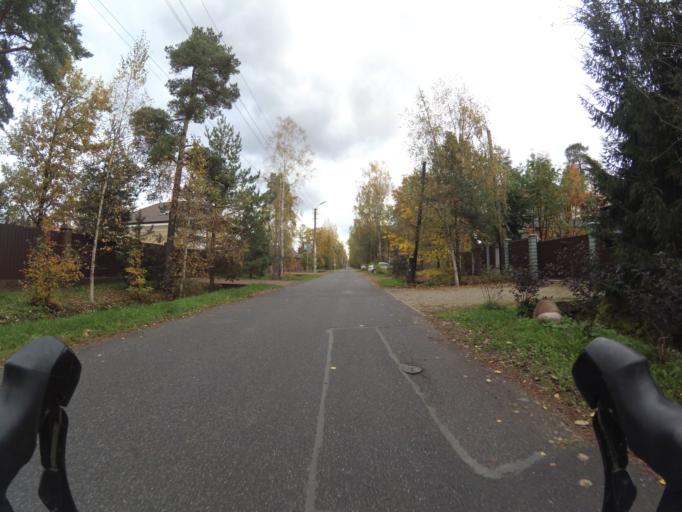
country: RU
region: St.-Petersburg
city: Lakhtinskiy
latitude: 59.9995
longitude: 30.1352
